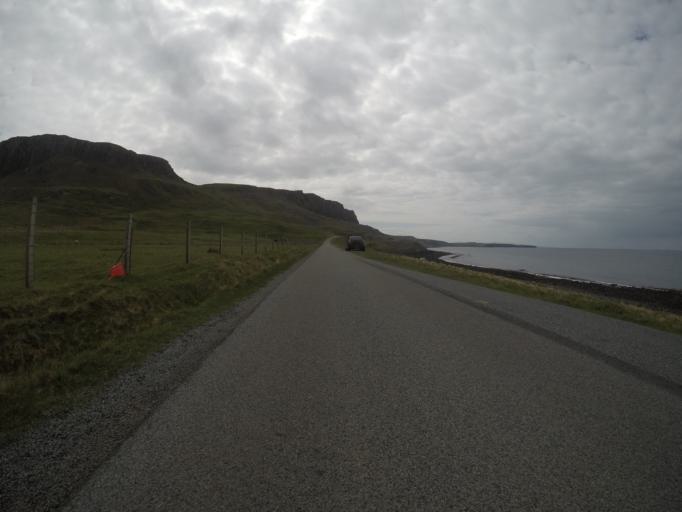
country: GB
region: Scotland
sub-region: Highland
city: Portree
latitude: 57.6782
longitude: -6.3457
